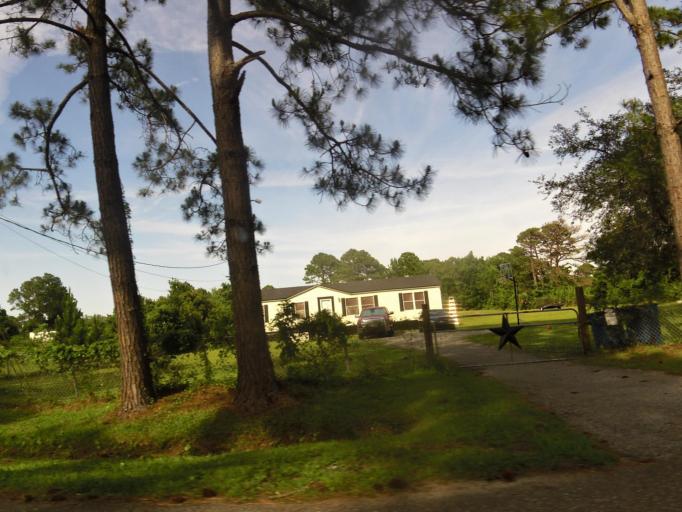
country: US
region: Florida
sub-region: Nassau County
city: Fernandina Beach
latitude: 30.5306
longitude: -81.4881
